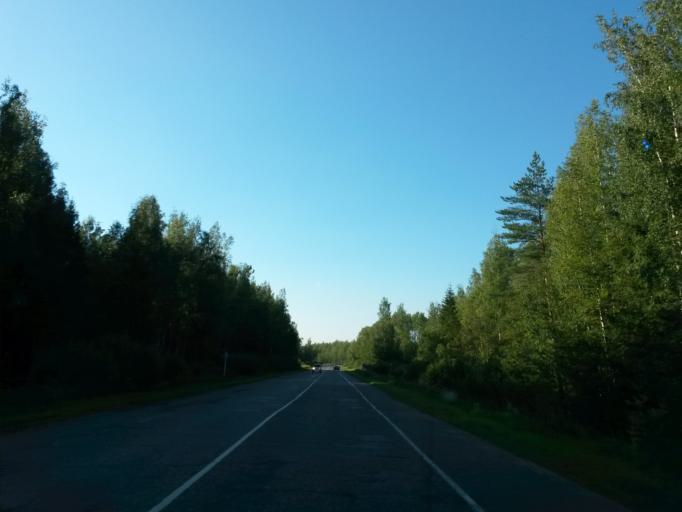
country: RU
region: Ivanovo
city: Pistsovo
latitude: 57.0835
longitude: 40.6724
